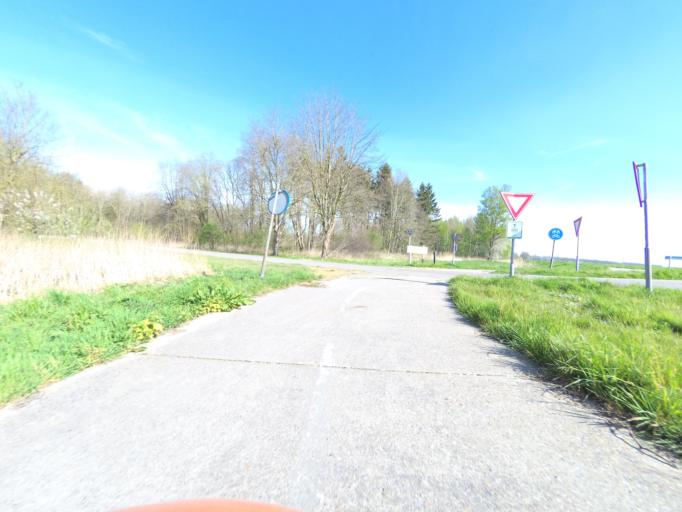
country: NL
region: Gelderland
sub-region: Gemeente Harderwijk
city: Harderwijk
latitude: 52.4400
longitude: 5.5748
